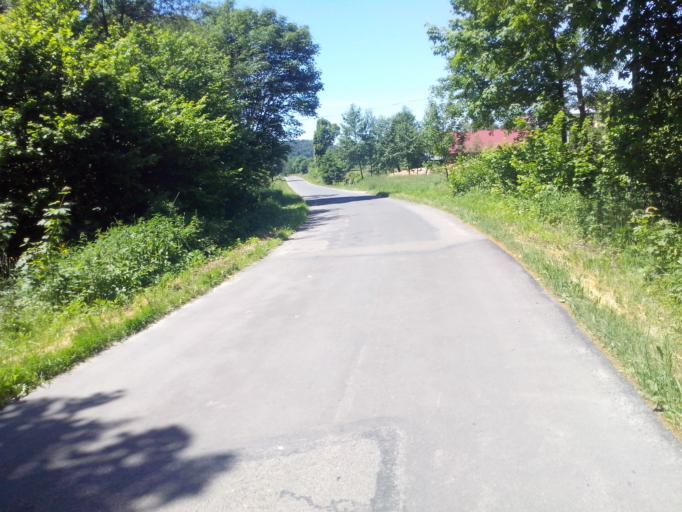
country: PL
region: Subcarpathian Voivodeship
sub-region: Powiat strzyzowski
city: Wysoka Strzyzowska
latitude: 49.7943
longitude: 21.7198
